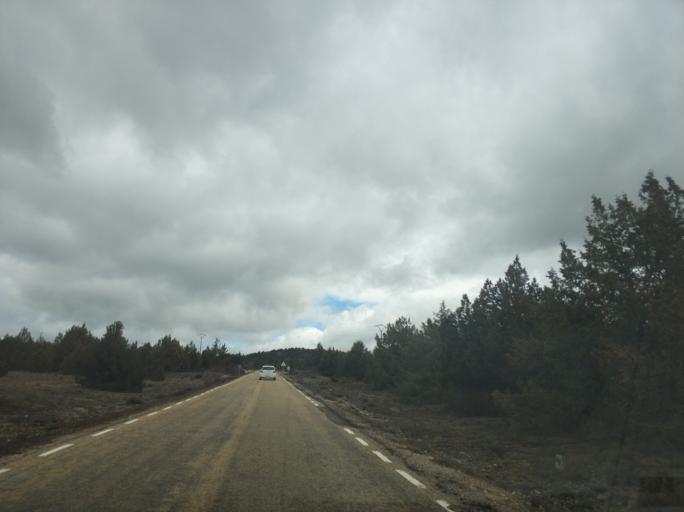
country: ES
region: Castille and Leon
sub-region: Provincia de Soria
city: Abejar
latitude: 41.7843
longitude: -2.7714
